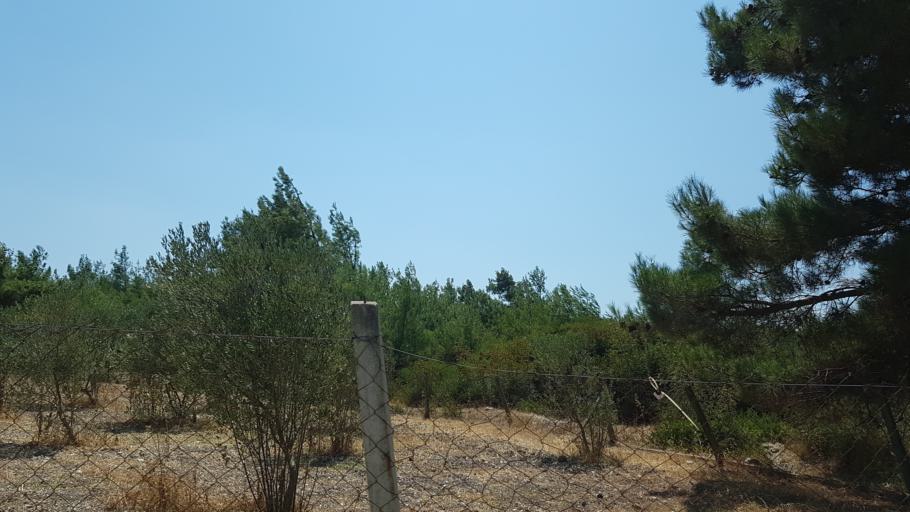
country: TR
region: Izmir
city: Urla
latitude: 38.2852
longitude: 26.7241
